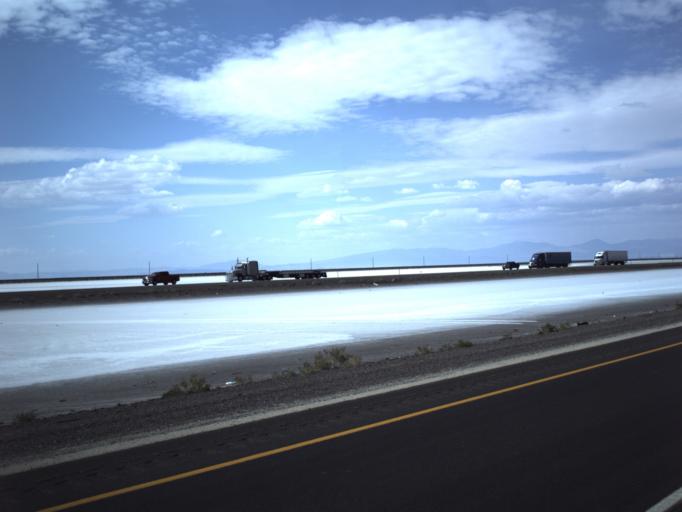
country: US
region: Utah
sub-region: Tooele County
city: Wendover
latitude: 40.7349
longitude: -113.6380
